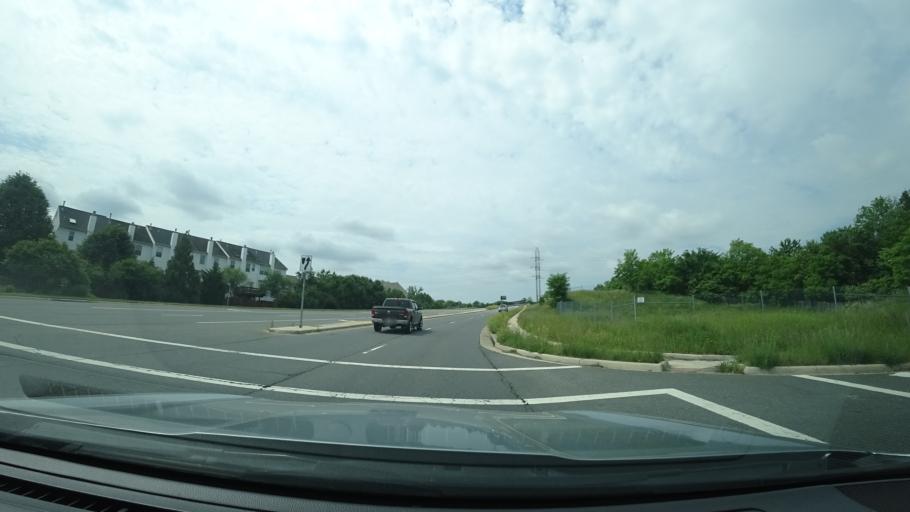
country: US
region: Virginia
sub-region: Loudoun County
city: Sterling
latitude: 39.0105
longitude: -77.4292
